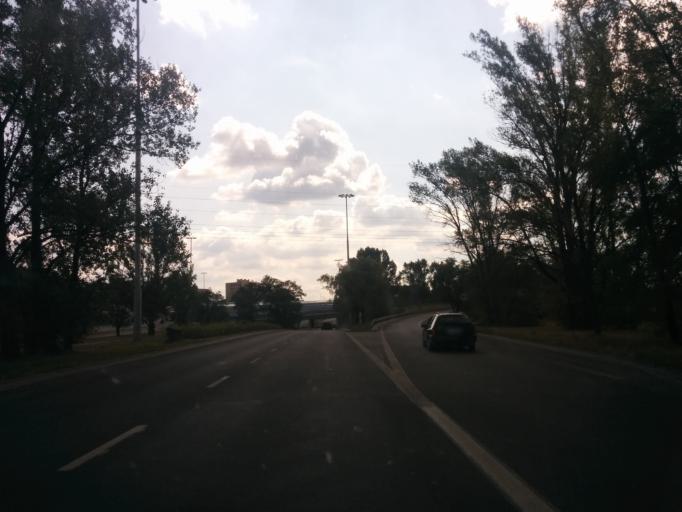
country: PL
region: Masovian Voivodeship
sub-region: Warszawa
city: Targowek
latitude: 52.2976
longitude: 21.0134
